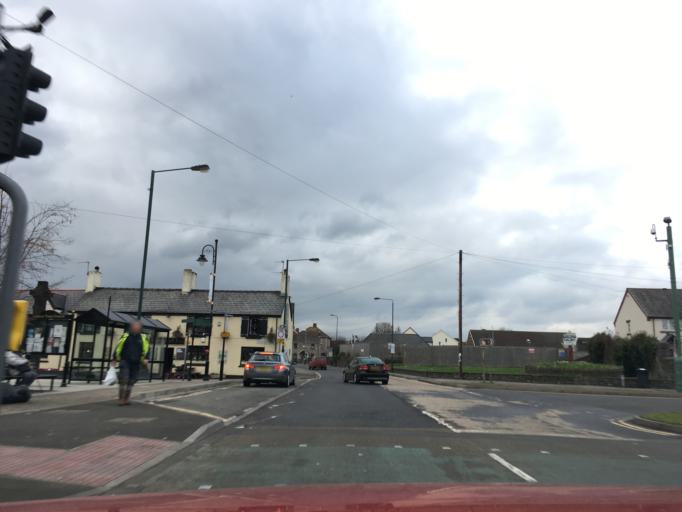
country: GB
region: Wales
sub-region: Monmouthshire
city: Caldicot
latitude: 51.5916
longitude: -2.7502
